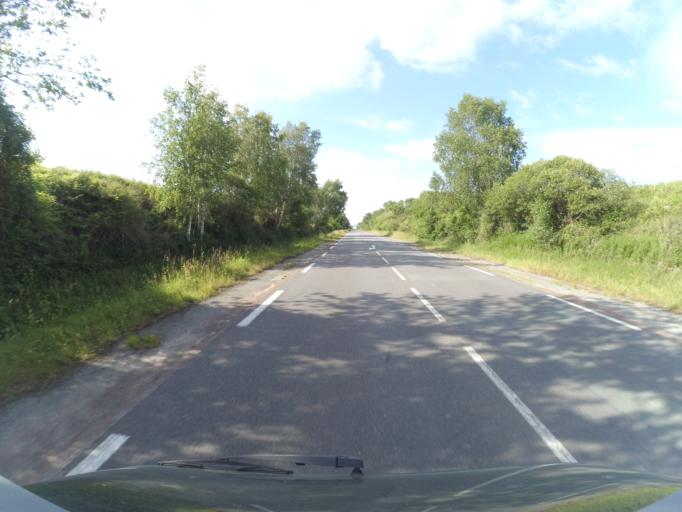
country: FR
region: Poitou-Charentes
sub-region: Departement de la Charente-Maritime
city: Le Gua
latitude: 45.7799
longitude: -0.9362
